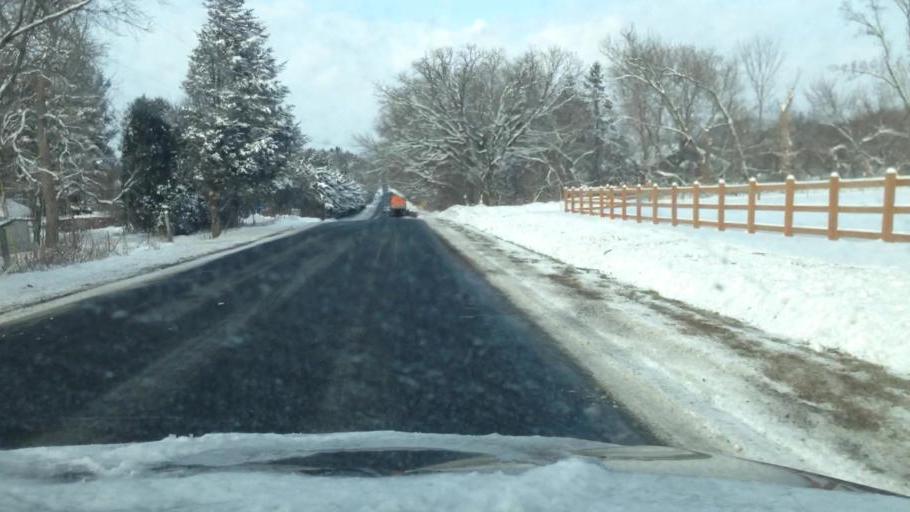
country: US
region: Wisconsin
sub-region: Walworth County
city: East Troy
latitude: 42.7594
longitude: -88.4457
